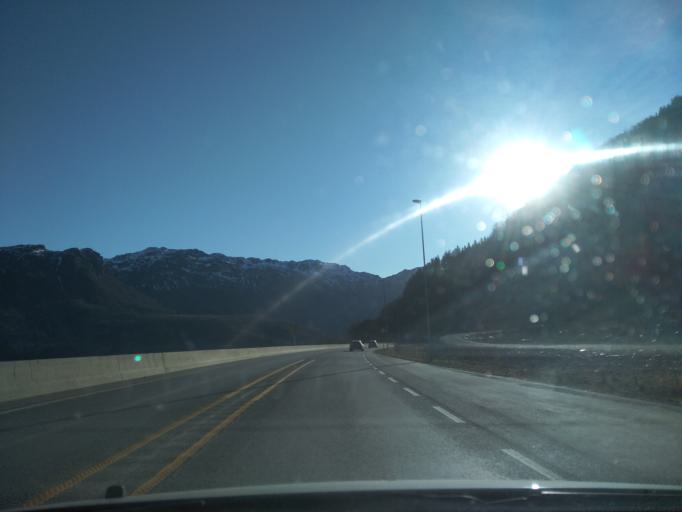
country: NO
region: Hordaland
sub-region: Etne
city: Etne
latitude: 59.7247
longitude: 6.1193
